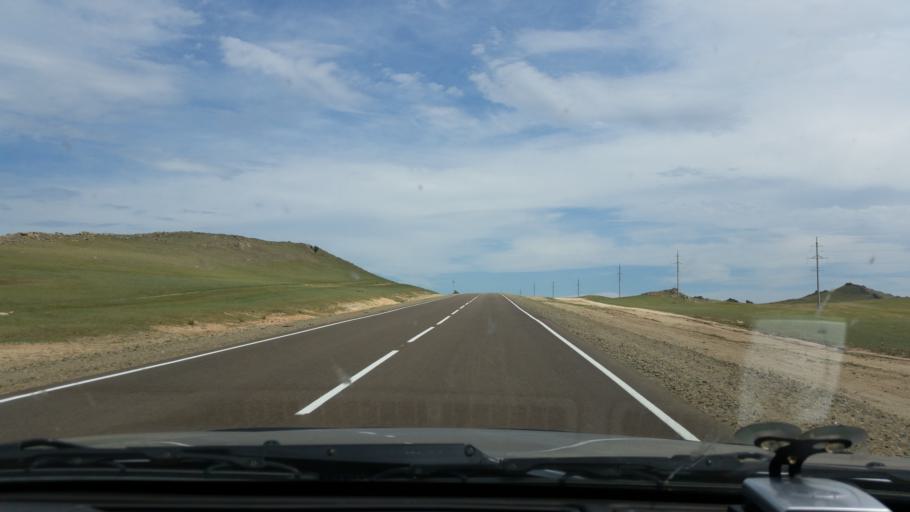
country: RU
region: Irkutsk
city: Yelantsy
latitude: 52.8862
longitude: 106.6013
